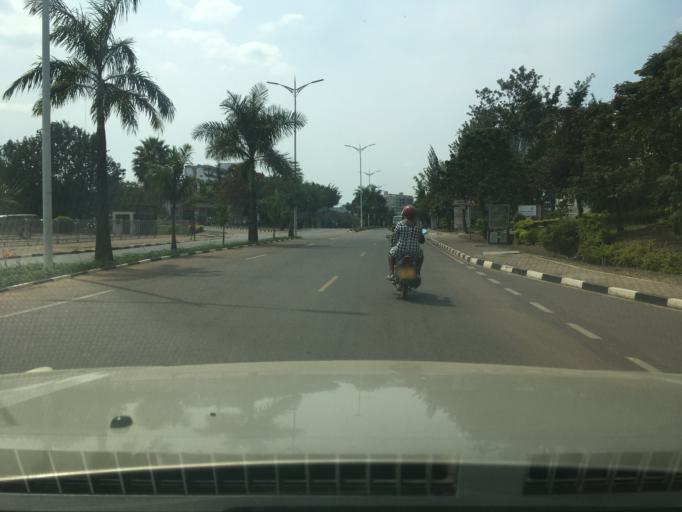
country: RW
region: Kigali
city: Kigali
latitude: -1.9540
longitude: 30.0961
